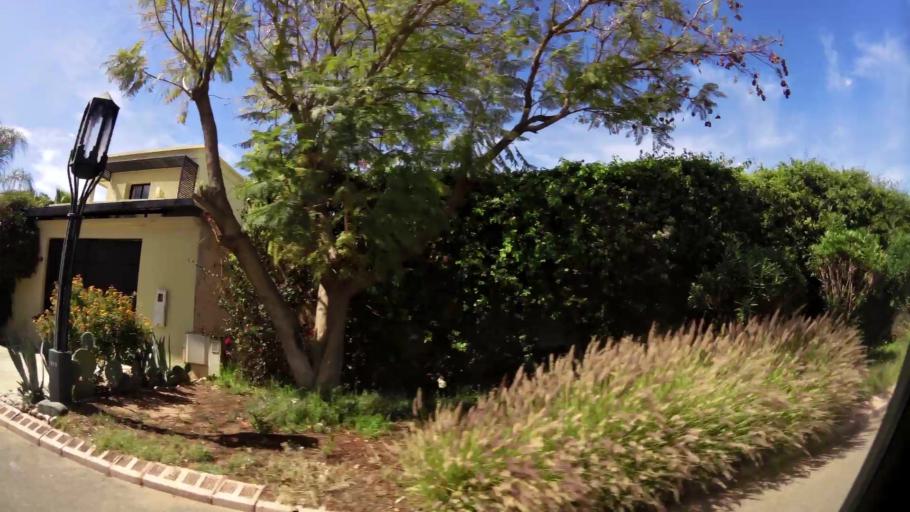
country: MA
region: Marrakech-Tensift-Al Haouz
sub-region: Marrakech
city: Marrakesh
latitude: 31.6179
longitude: -7.9349
